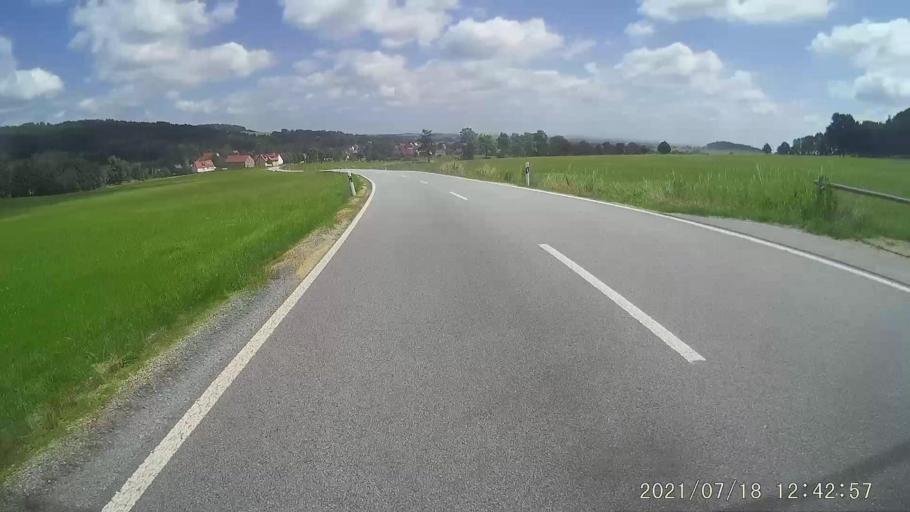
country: DE
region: Saxony
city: Konigshain
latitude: 51.1849
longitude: 14.8356
